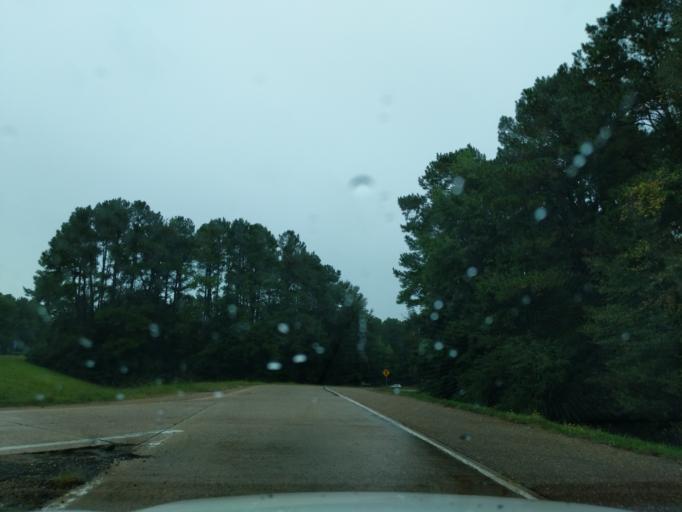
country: US
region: Louisiana
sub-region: Bienville Parish
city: Arcadia
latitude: 32.5618
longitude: -93.0539
